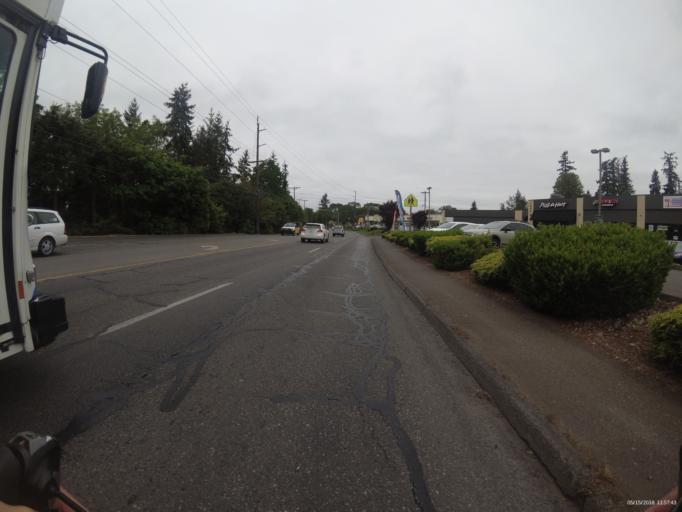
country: US
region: Washington
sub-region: Pierce County
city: Lakewood
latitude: 47.1785
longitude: -122.5389
